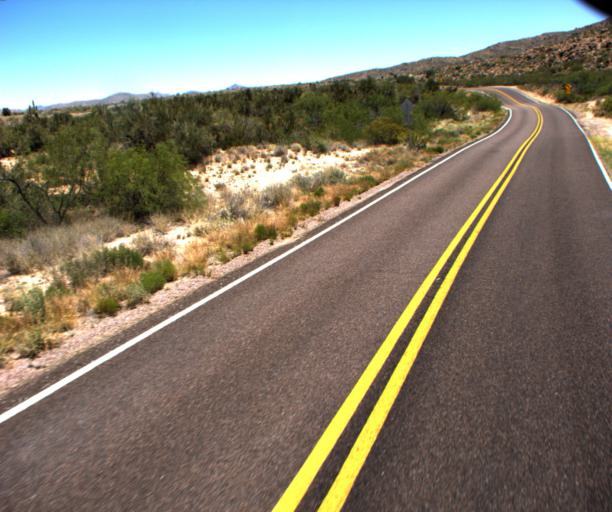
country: US
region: Arizona
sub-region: Yavapai County
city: Bagdad
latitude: 34.5003
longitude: -113.1679
